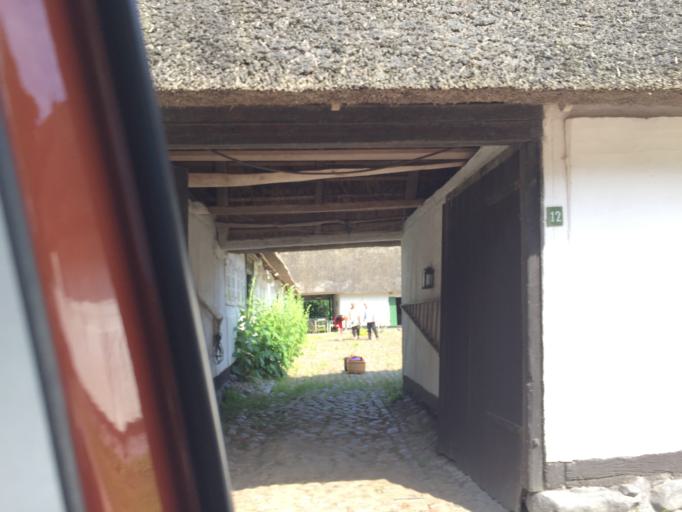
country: DK
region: South Denmark
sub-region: Kerteminde Kommune
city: Kerteminde
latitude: 55.4976
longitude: 10.6861
